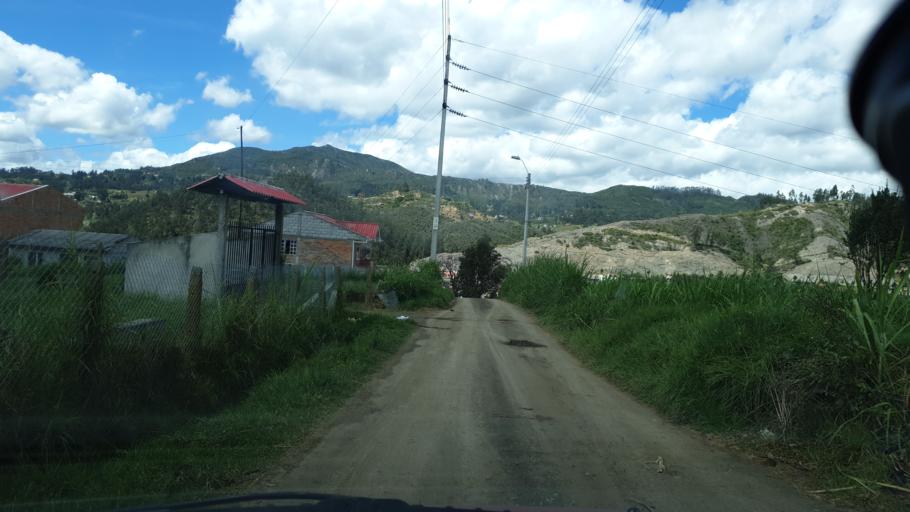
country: EC
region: Azuay
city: Cuenca
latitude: -2.8741
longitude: -78.9493
